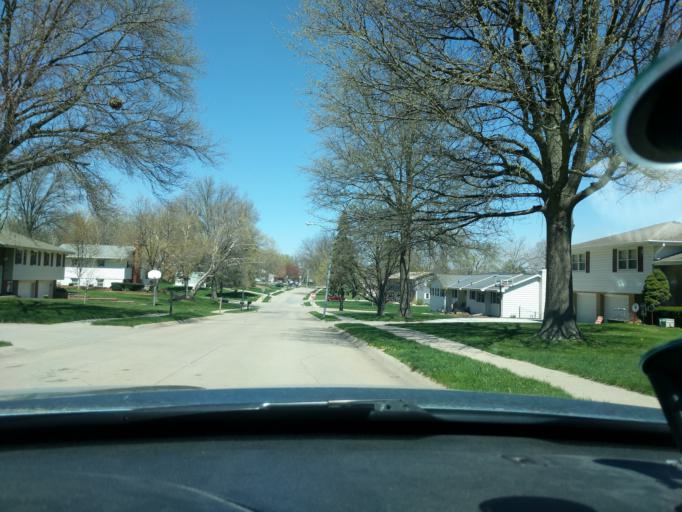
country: US
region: Nebraska
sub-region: Douglas County
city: Ralston
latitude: 41.2277
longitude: -96.0965
